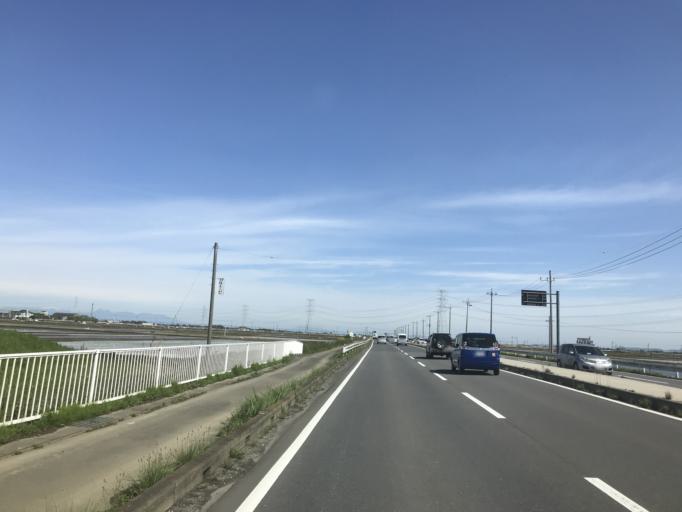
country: JP
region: Ibaraki
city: Ishige
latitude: 36.1152
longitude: 139.9832
